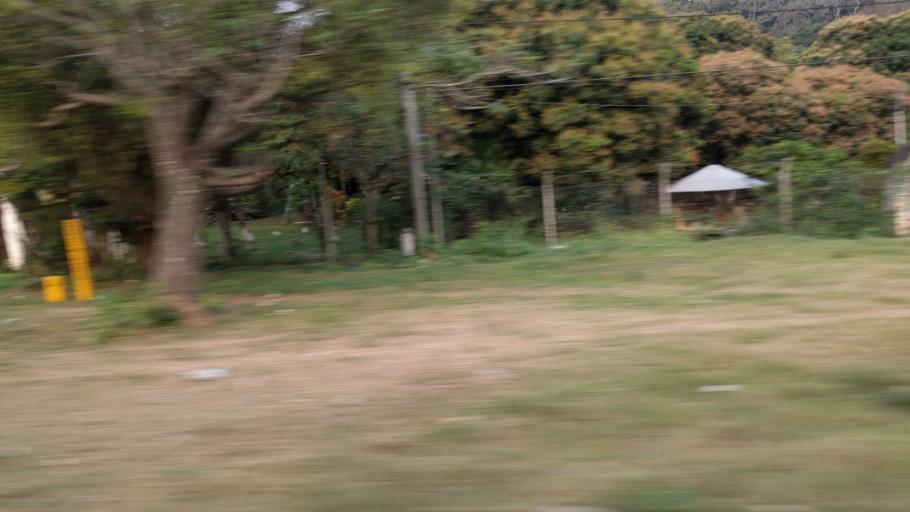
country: BO
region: Santa Cruz
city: Santa Rita
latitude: -17.9315
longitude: -63.3484
